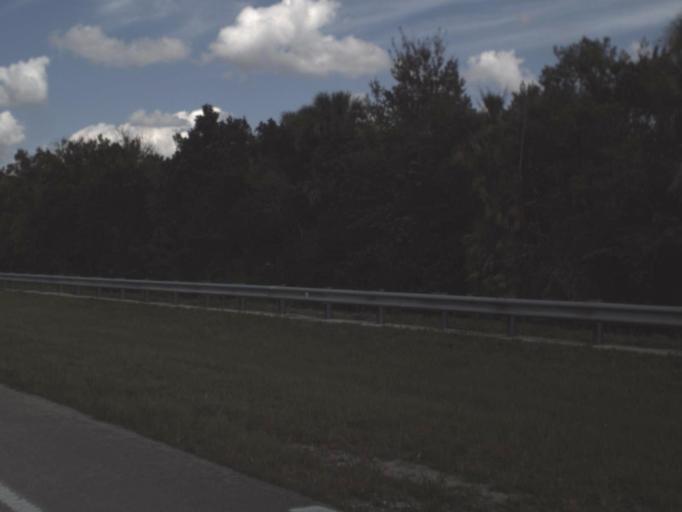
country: US
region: Florida
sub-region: Collier County
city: Orangetree
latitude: 26.0706
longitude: -81.3446
